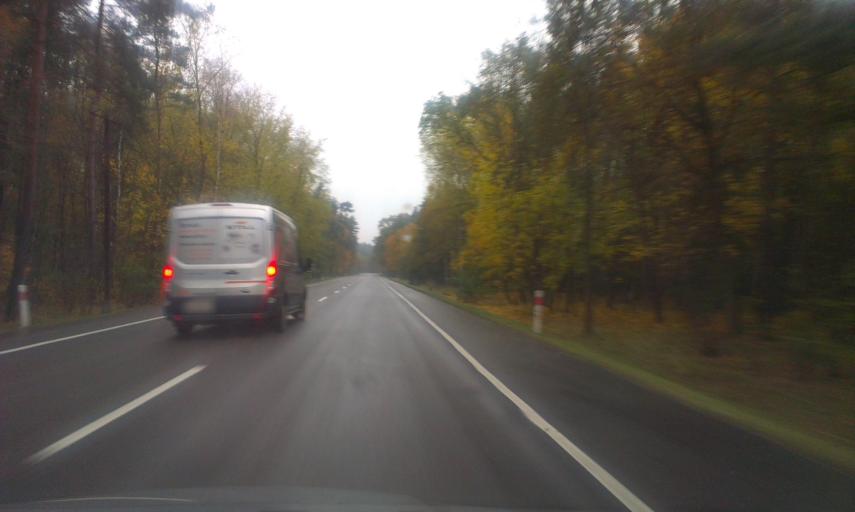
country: PL
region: Greater Poland Voivodeship
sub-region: Powiat chodzieski
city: Budzyn
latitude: 52.8412
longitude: 16.9715
